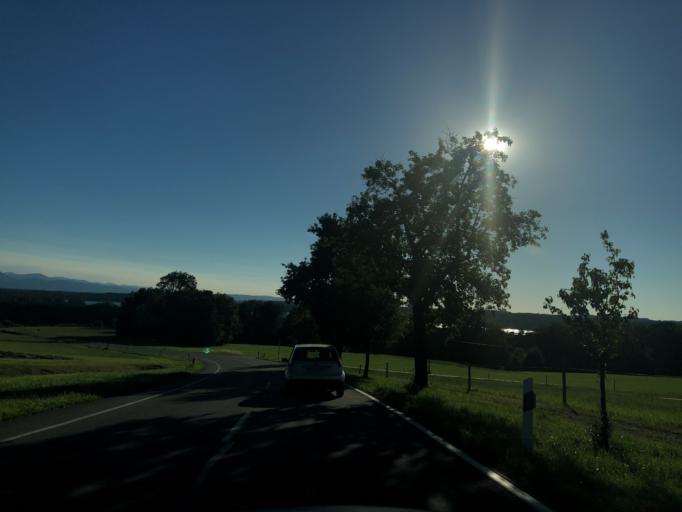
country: DE
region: Bavaria
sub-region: Upper Bavaria
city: Riedering
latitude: 47.8642
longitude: 12.2494
